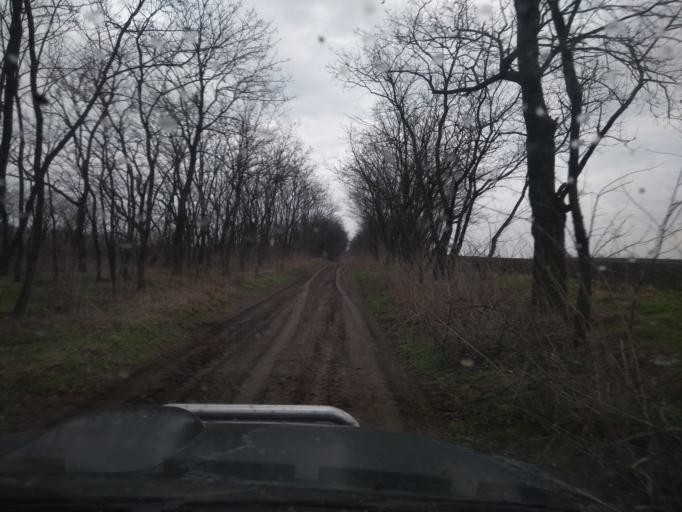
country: HU
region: Szabolcs-Szatmar-Bereg
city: Nagycserkesz
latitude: 47.9805
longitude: 21.5514
